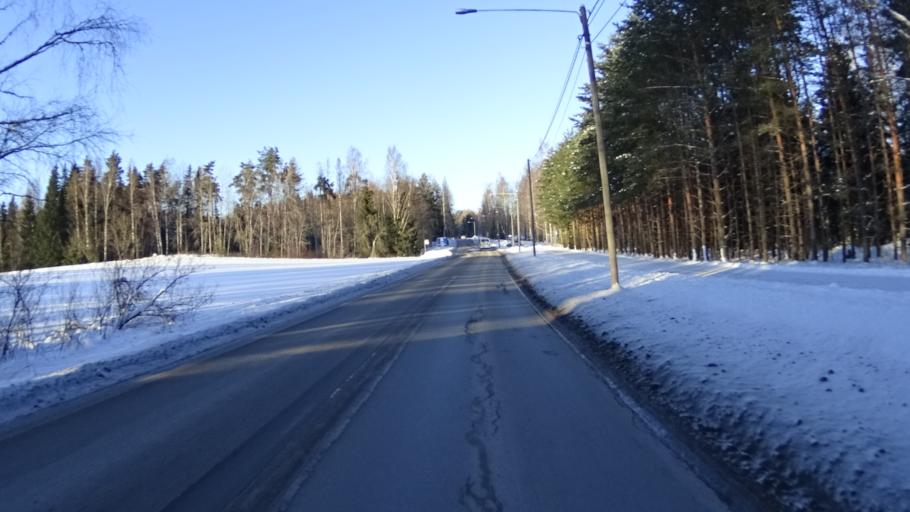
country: FI
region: Uusimaa
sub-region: Helsinki
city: Espoo
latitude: 60.2372
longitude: 24.6553
